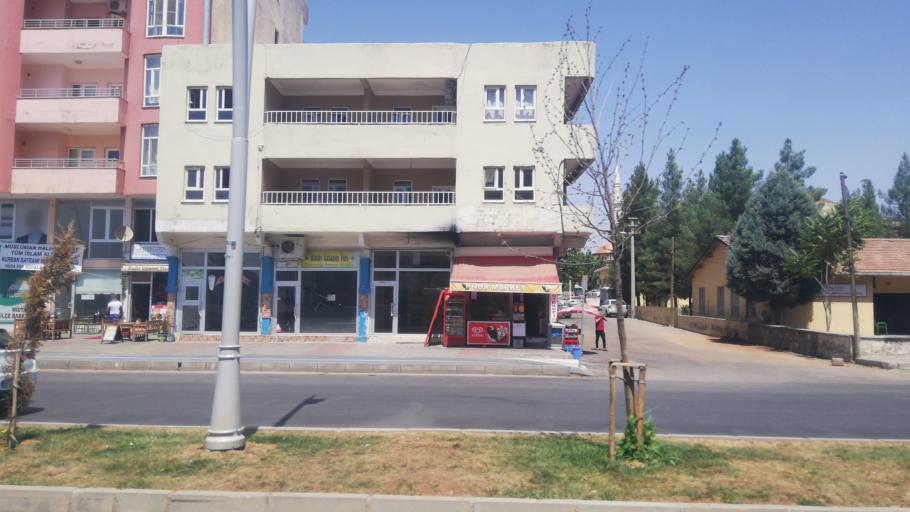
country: TR
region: Mardin
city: Midyat
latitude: 37.4205
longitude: 41.3510
